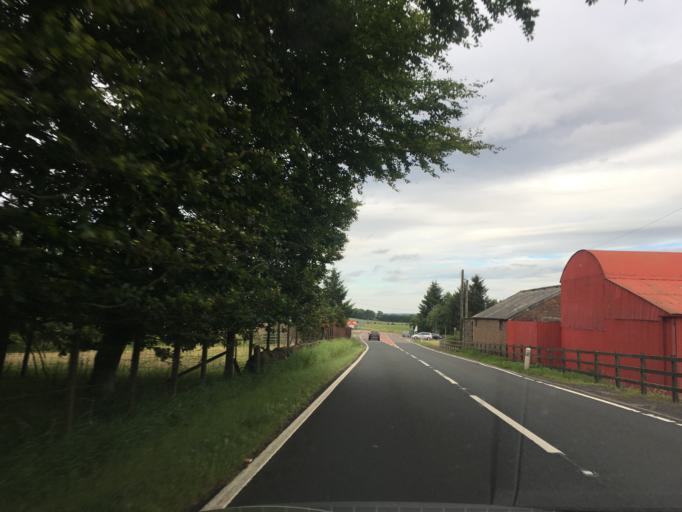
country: GB
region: Scotland
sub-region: South Lanarkshire
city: Biggar
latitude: 55.6818
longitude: -3.4552
